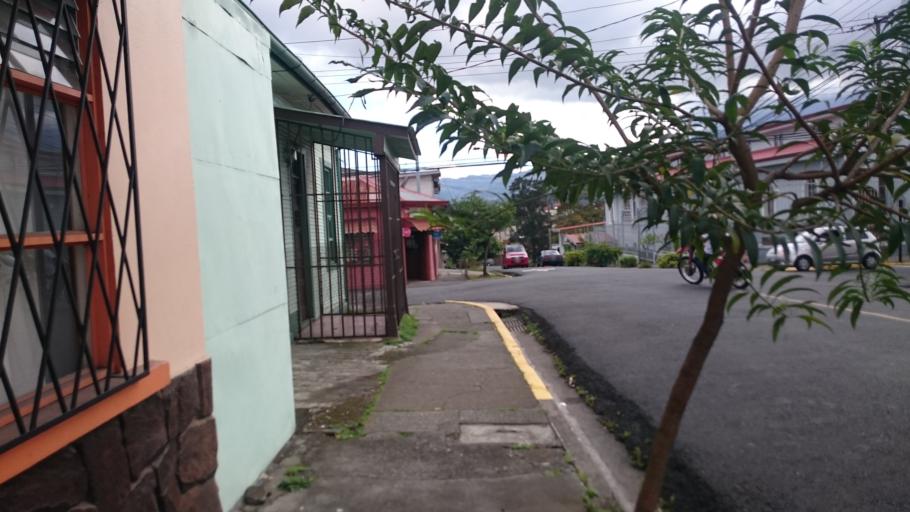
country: CR
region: San Jose
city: San Jose
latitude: 9.9212
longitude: -84.0784
